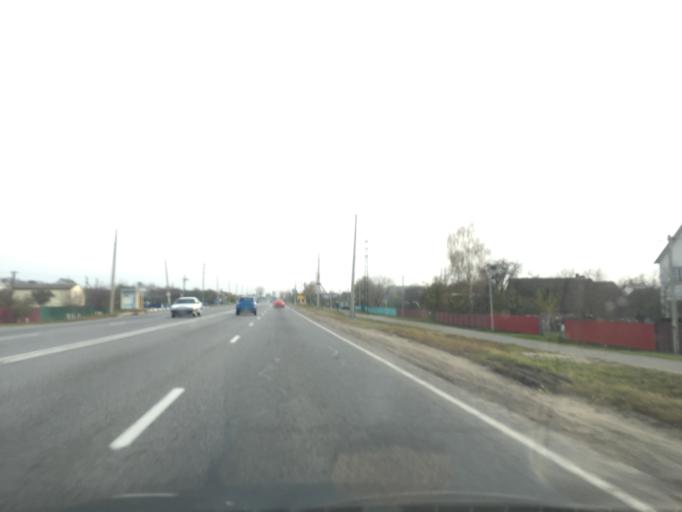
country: BY
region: Gomel
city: Kastsyukowka
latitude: 52.4954
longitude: 30.9593
